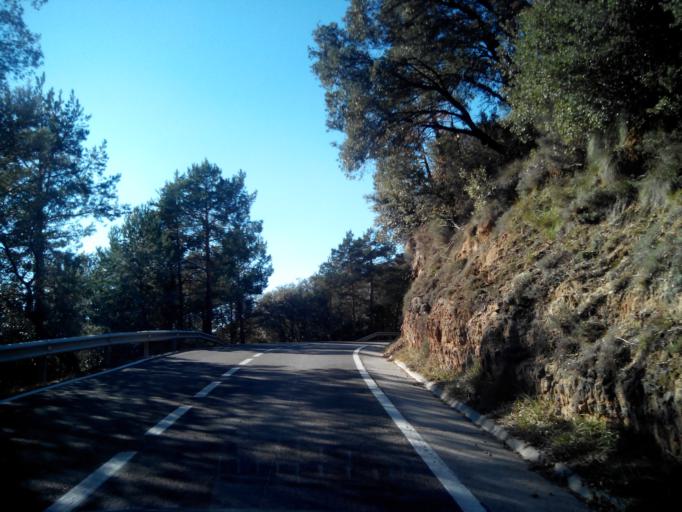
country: ES
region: Catalonia
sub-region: Provincia de Barcelona
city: Castellar del Riu
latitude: 42.0961
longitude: 1.7924
